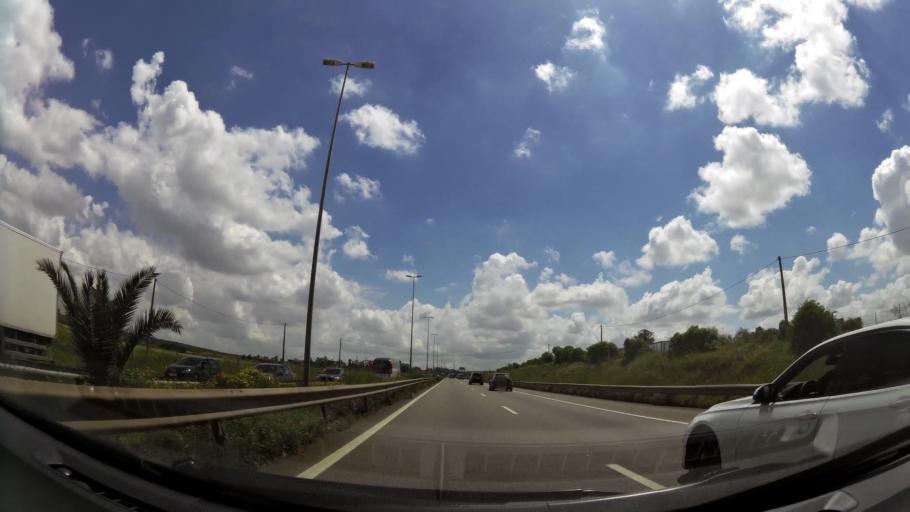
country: MA
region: Grand Casablanca
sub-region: Nouaceur
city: Bouskoura
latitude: 33.4441
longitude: -7.6317
